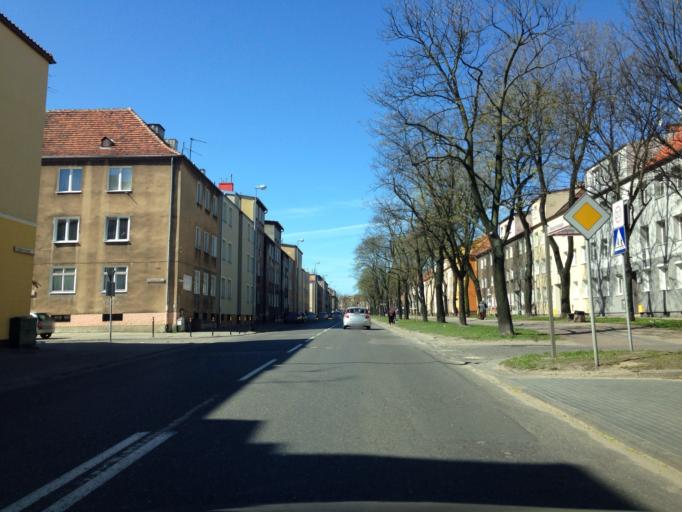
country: PL
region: Pomeranian Voivodeship
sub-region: Gdansk
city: Gdansk
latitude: 54.3879
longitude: 18.6212
